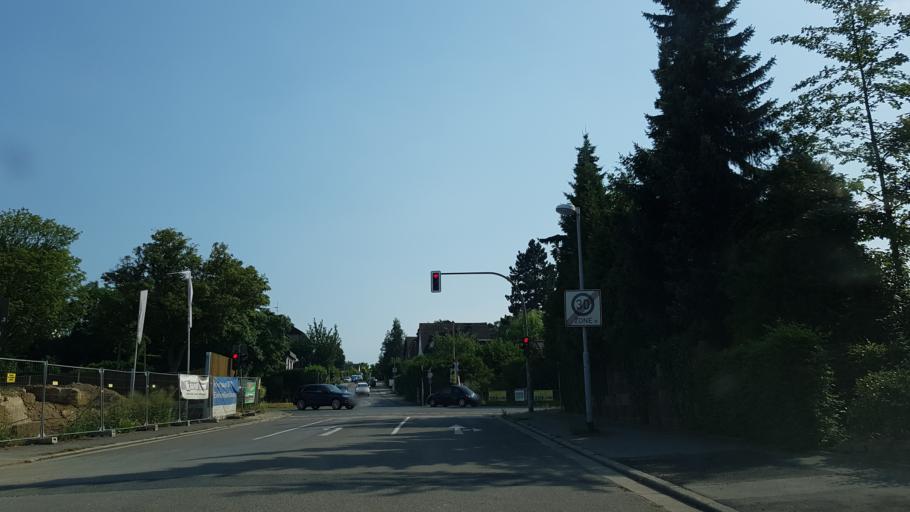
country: DE
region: North Rhine-Westphalia
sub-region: Regierungsbezirk Dusseldorf
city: Muelheim (Ruhr)
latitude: 51.4099
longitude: 6.9324
